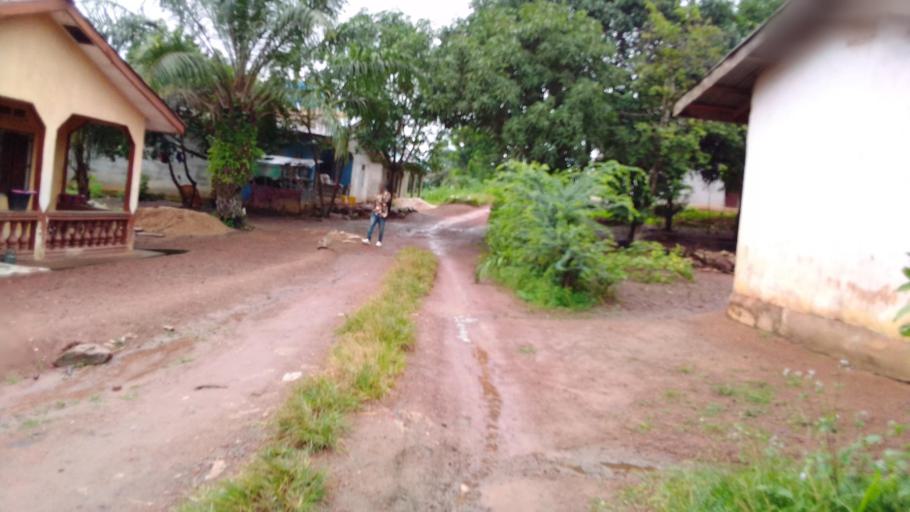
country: SL
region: Eastern Province
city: Kenema
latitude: 7.8706
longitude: -11.1739
